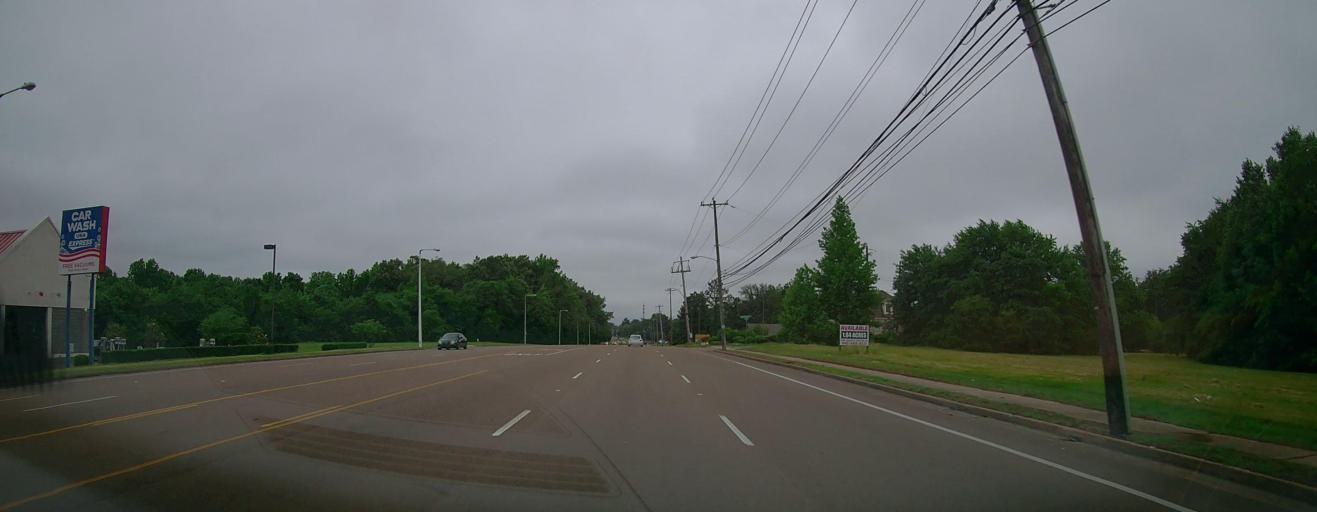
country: US
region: Tennessee
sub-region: Shelby County
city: Germantown
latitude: 35.0465
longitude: -89.8305
